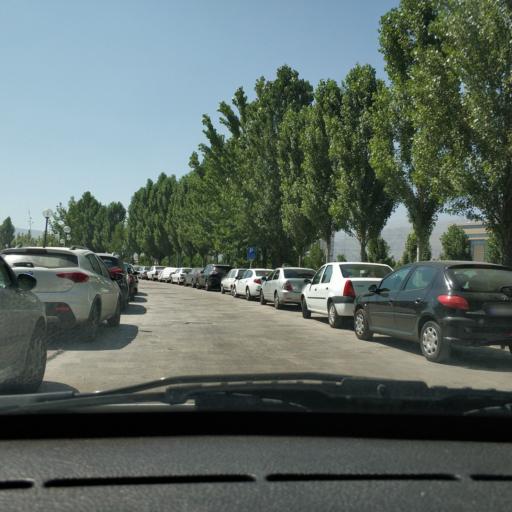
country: IR
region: Tehran
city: Tajrish
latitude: 35.7563
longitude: 51.4341
